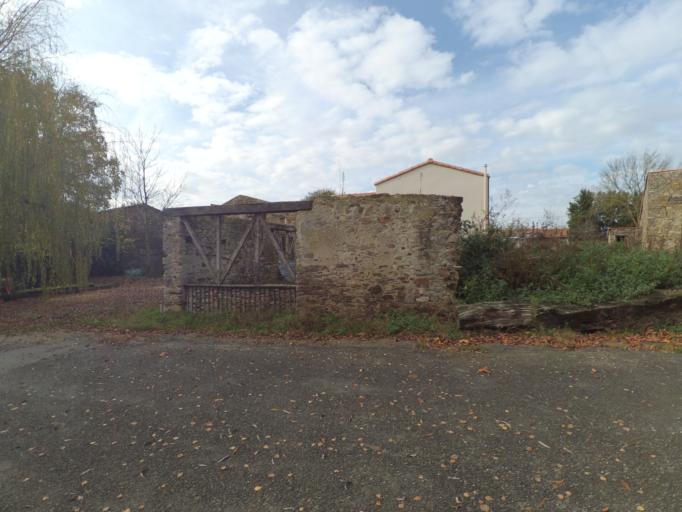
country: FR
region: Pays de la Loire
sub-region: Departement de la Loire-Atlantique
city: La Planche
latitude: 46.9963
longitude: -1.3989
